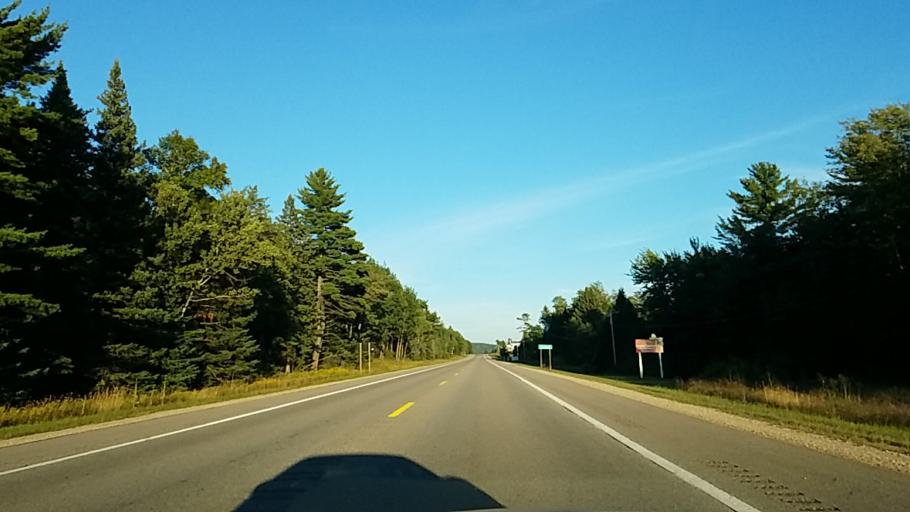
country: US
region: Michigan
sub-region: Alger County
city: Munising
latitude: 46.4416
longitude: -86.7272
